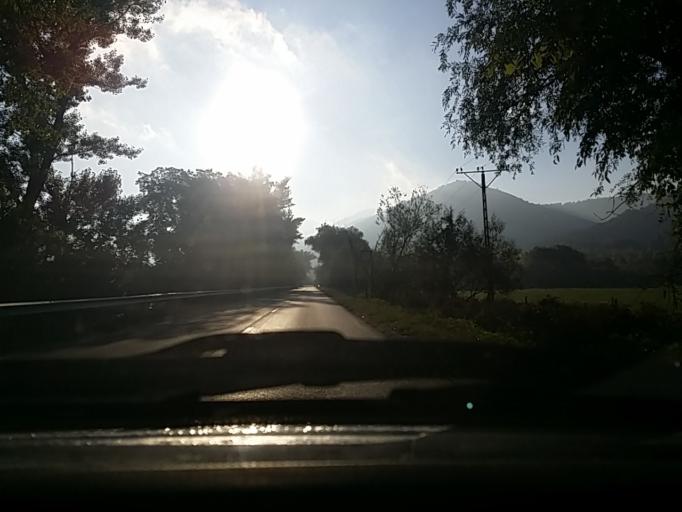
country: HU
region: Pest
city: Nagymaros
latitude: 47.7636
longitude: 18.9222
